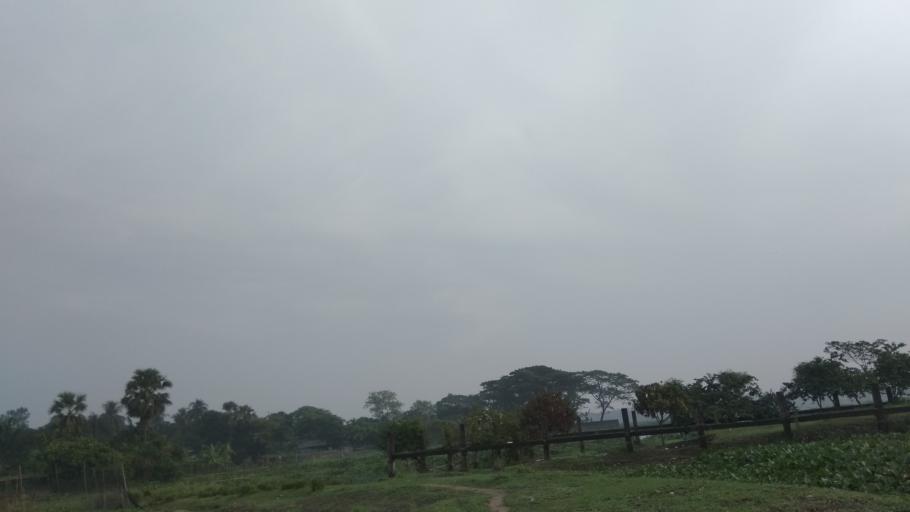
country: BD
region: Dhaka
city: Tungi
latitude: 23.8519
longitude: 90.4460
